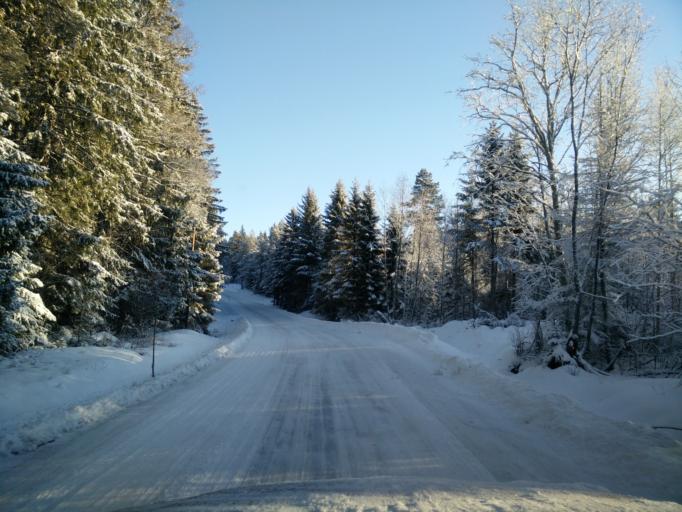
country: SE
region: Vaesternorrland
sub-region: Sundsvalls Kommun
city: Njurundabommen
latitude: 62.2358
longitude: 17.6079
